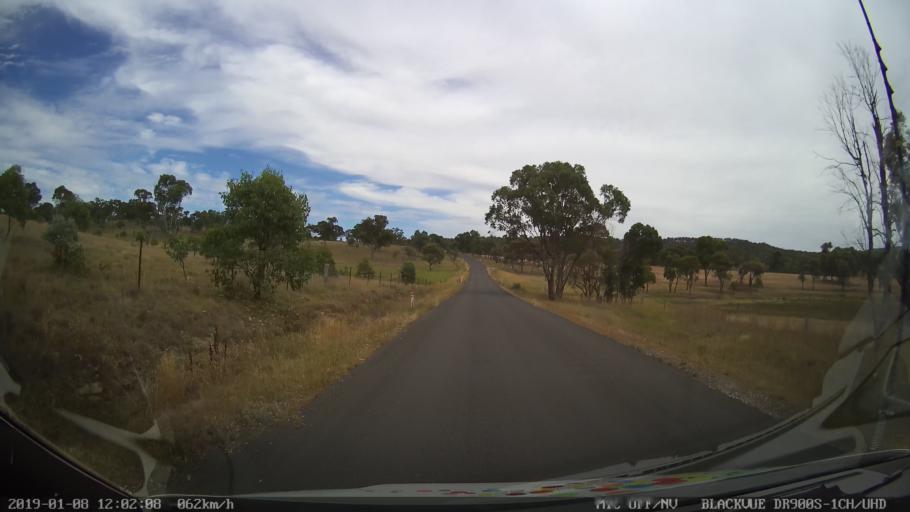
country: AU
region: New South Wales
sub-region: Armidale Dumaresq
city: Armidale
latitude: -30.4563
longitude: 151.6061
